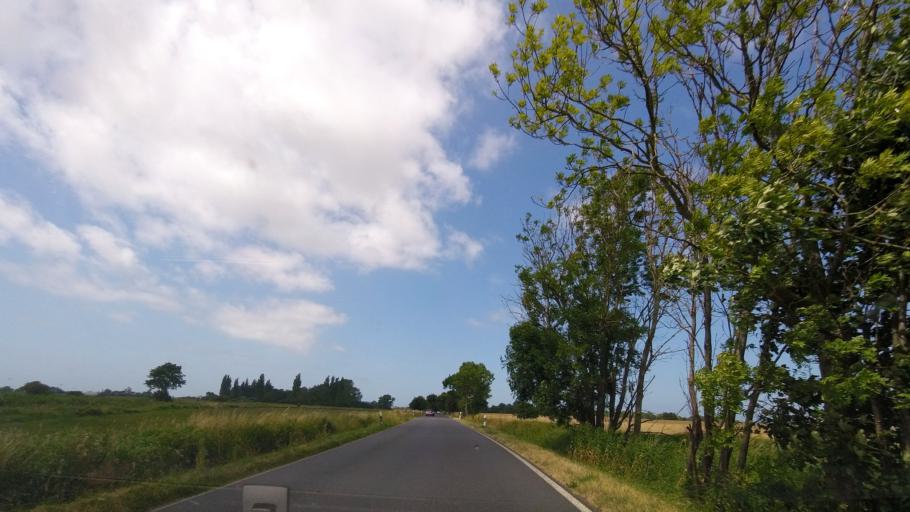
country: DE
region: Mecklenburg-Vorpommern
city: Wiek
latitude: 54.6405
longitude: 13.3047
